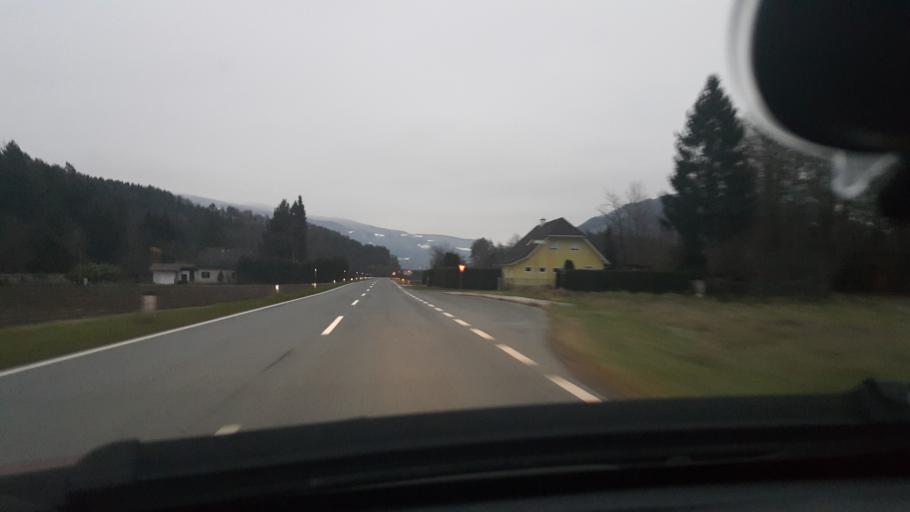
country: AT
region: Carinthia
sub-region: Politischer Bezirk Volkermarkt
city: Neuhaus
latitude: 46.6569
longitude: 14.8792
